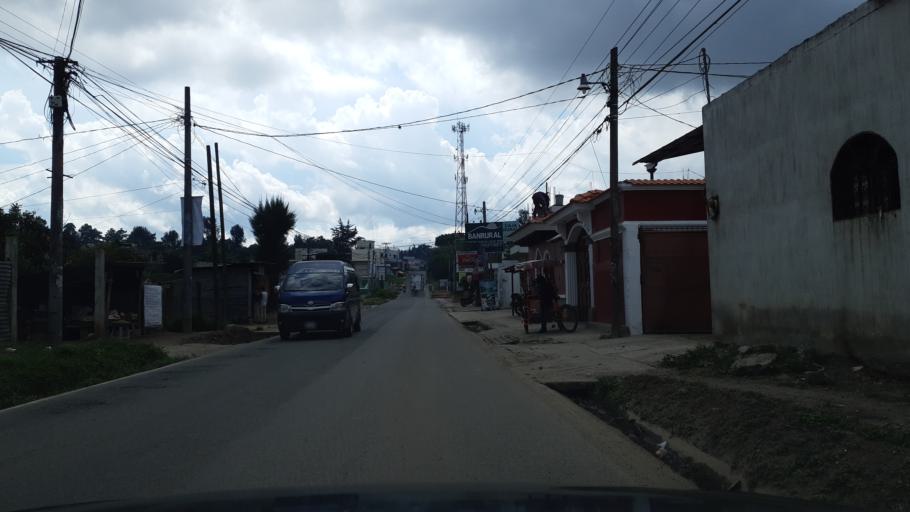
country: GT
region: Chimaltenango
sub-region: Municipio de Chimaltenango
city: Chimaltenango
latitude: 14.6764
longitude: -90.8013
